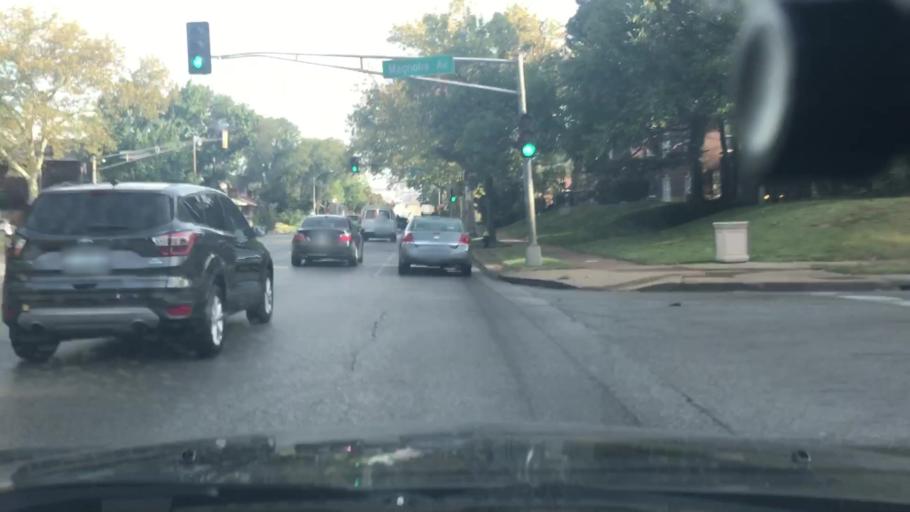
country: US
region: Missouri
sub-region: Saint Louis County
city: Richmond Heights
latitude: 38.6097
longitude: -90.2682
